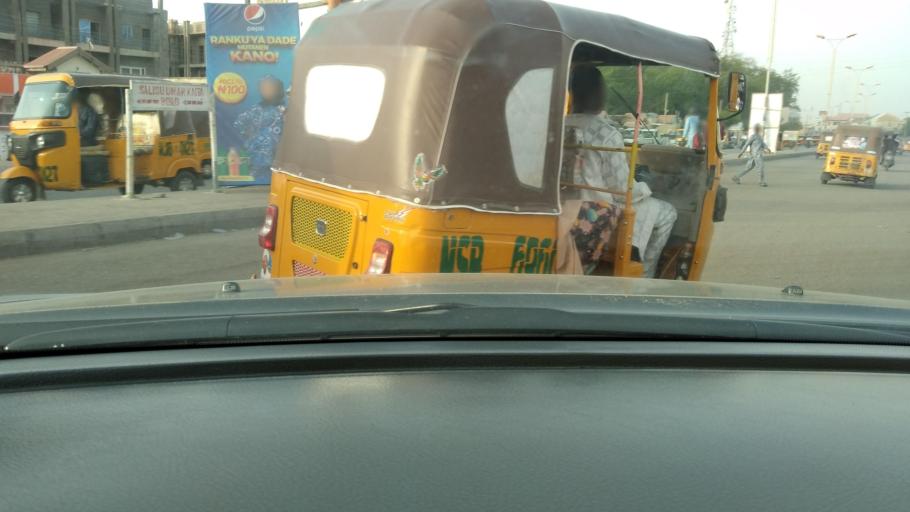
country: NG
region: Kano
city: Kano
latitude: 11.9636
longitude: 8.5257
